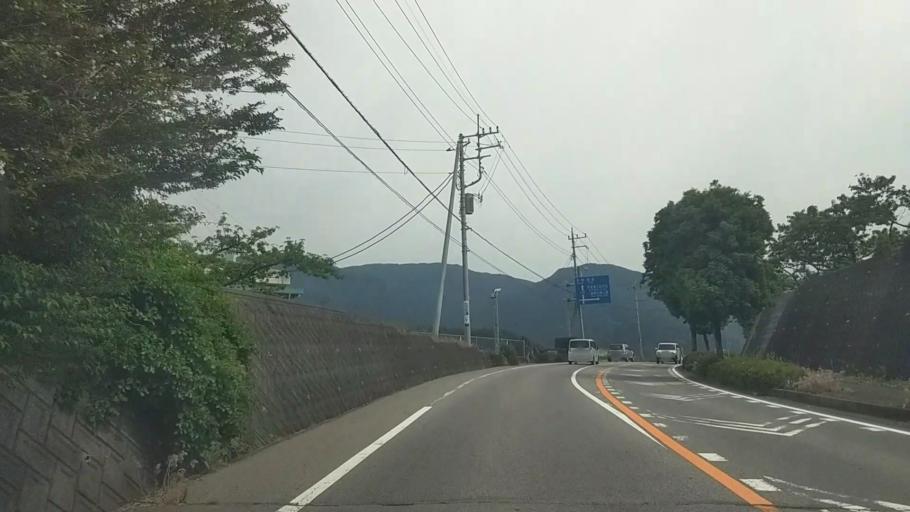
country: JP
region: Yamanashi
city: Isawa
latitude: 35.5855
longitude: 138.5904
